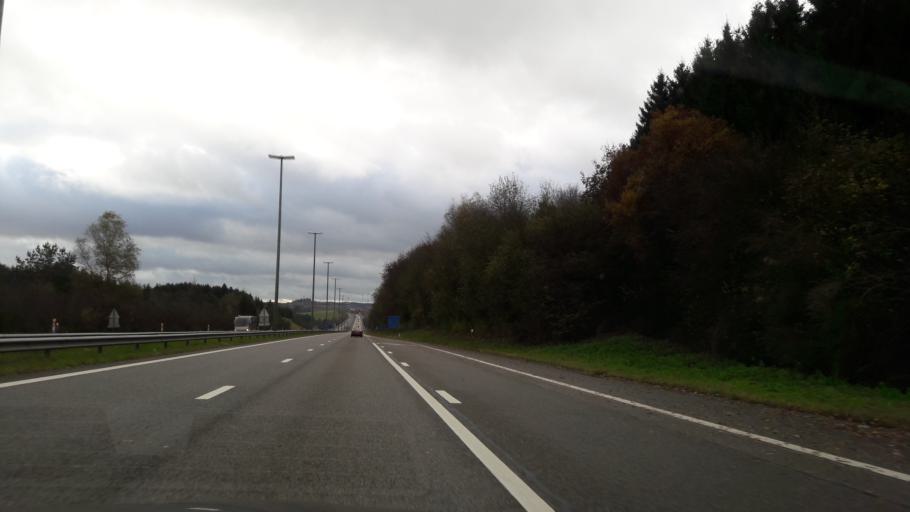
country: DE
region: Rheinland-Pfalz
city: Winterspelt
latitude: 50.2480
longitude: 6.1734
